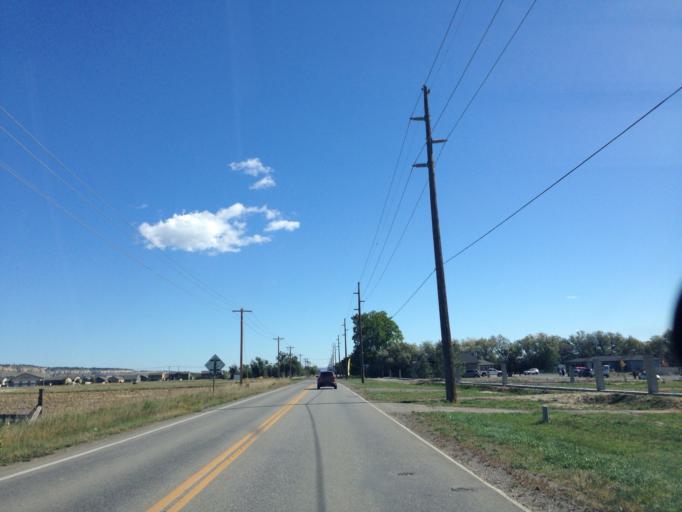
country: US
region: Montana
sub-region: Yellowstone County
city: Billings
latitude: 45.7841
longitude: -108.6581
